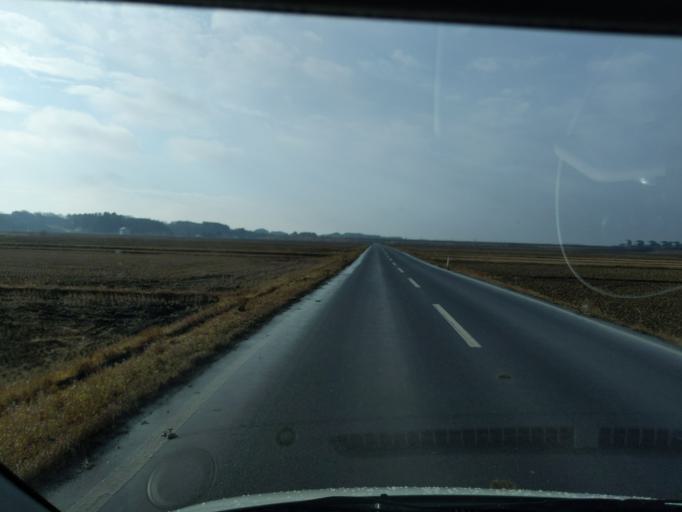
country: JP
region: Miyagi
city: Wakuya
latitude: 38.7171
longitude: 141.1586
